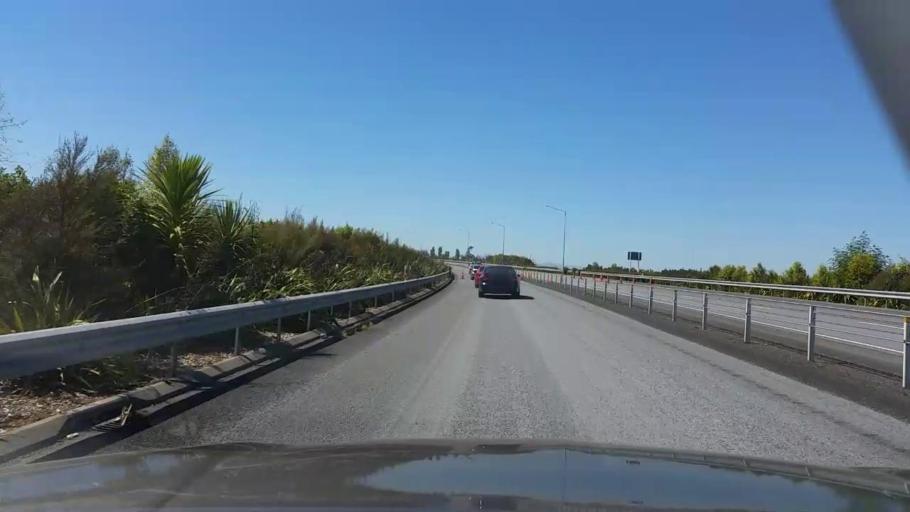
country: NZ
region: Waikato
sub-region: Hamilton City
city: Hamilton
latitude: -37.7514
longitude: 175.2193
